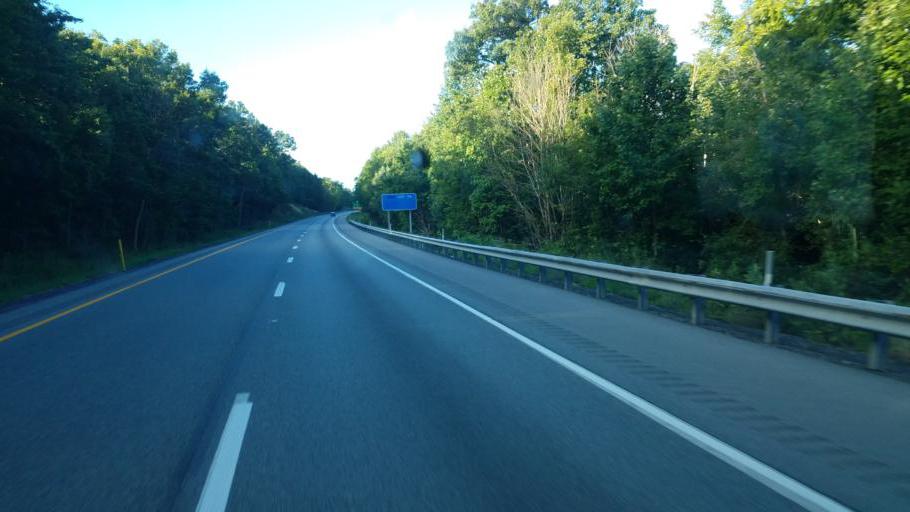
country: US
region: Pennsylvania
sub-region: Bedford County
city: Earlston
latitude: 39.9028
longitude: -78.2392
